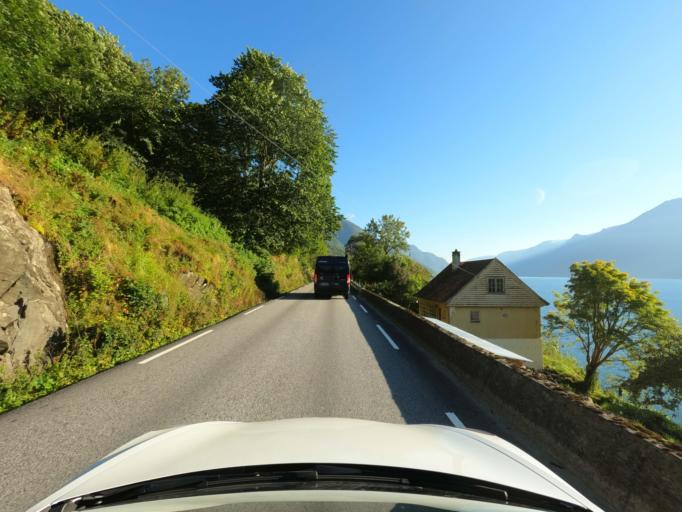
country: NO
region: Hordaland
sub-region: Ullensvang
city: Kinsarvik
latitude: 60.2702
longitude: 6.6207
